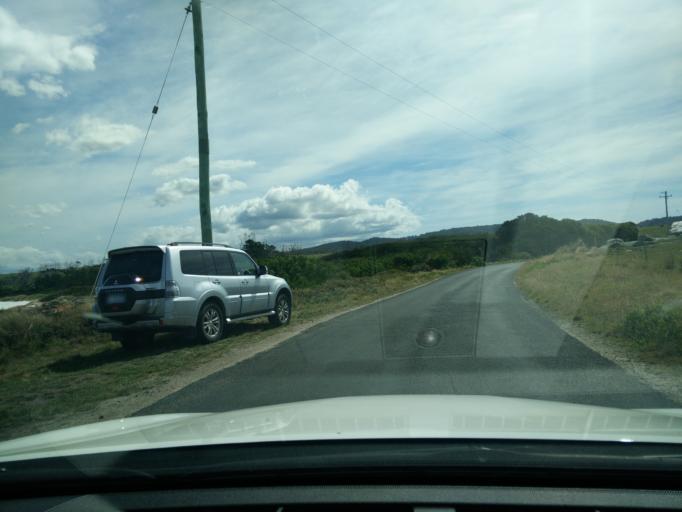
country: AU
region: Tasmania
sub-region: Break O'Day
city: St Helens
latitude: -41.1688
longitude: 148.2825
